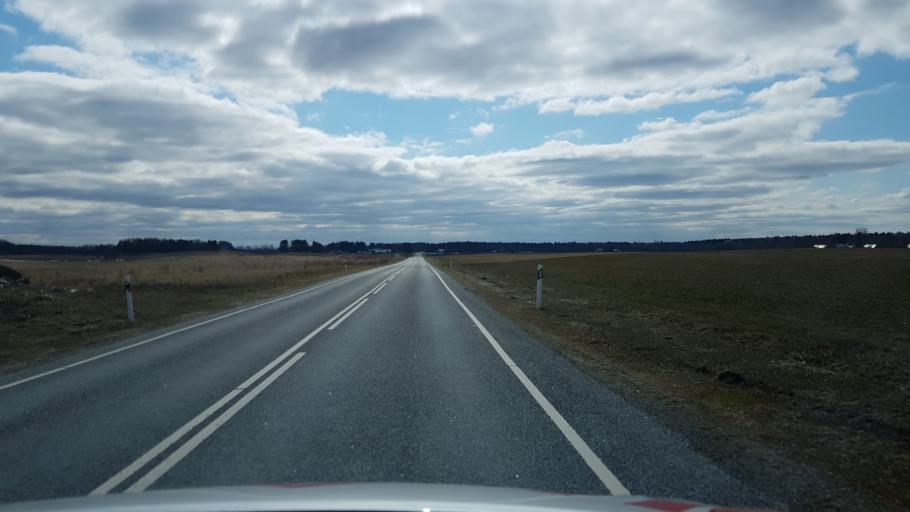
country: EE
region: Laeaene-Virumaa
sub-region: Tapa vald
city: Tapa
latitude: 59.3024
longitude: 25.9996
